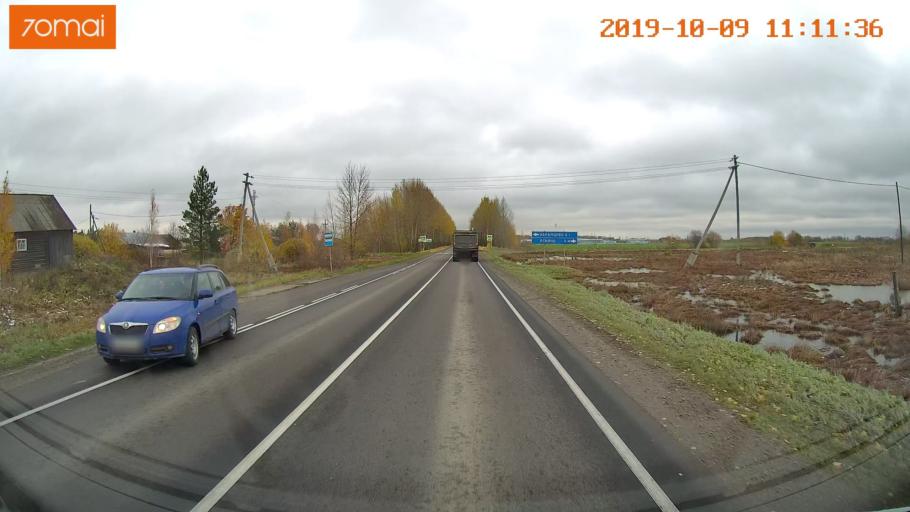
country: RU
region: Vologda
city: Vologda
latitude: 59.1697
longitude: 39.8222
